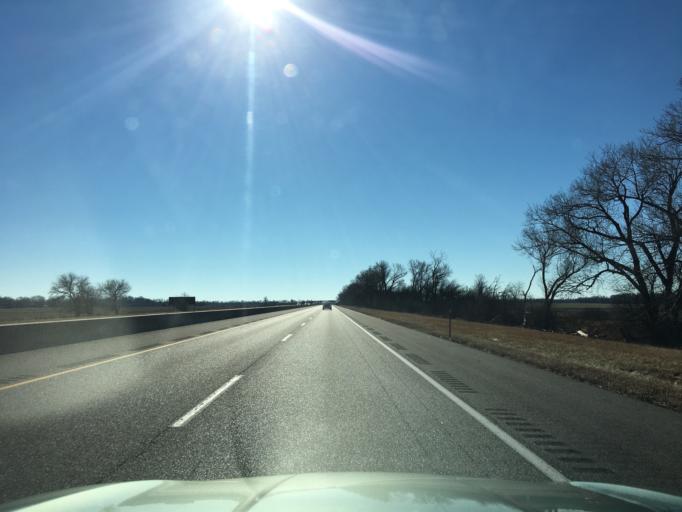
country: US
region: Kansas
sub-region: Sumner County
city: Belle Plaine
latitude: 37.4454
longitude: -97.3220
